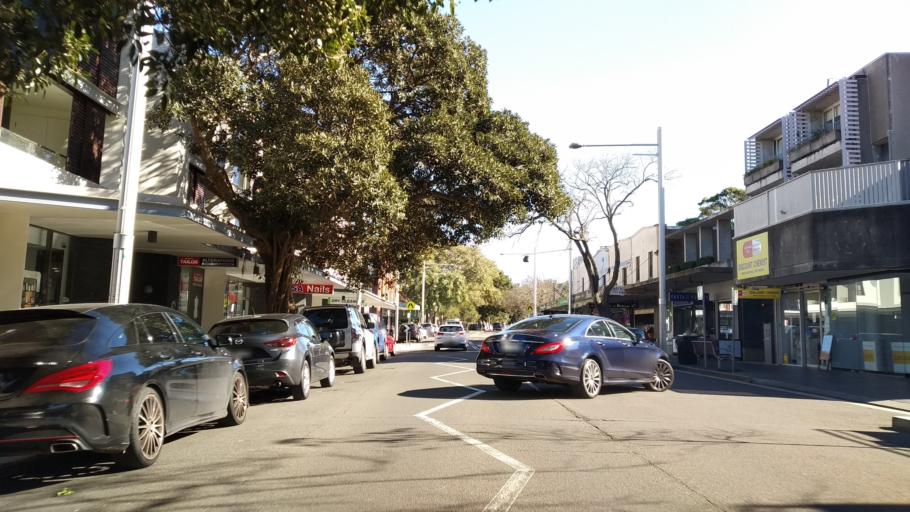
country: AU
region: New South Wales
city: Edgecliff
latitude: -33.8863
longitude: 151.2578
